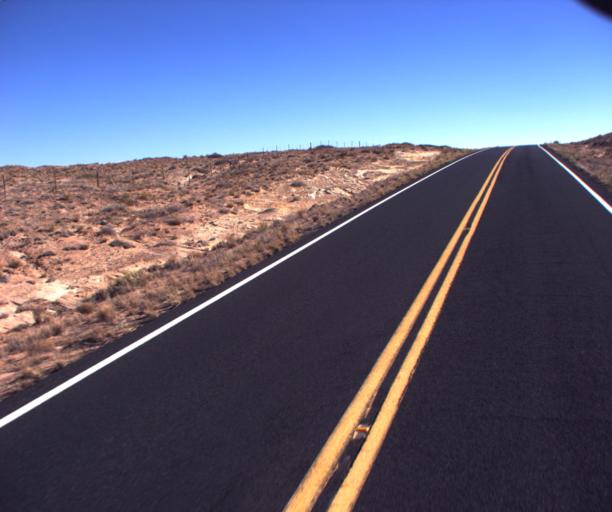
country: US
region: Arizona
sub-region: Coconino County
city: Tuba City
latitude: 36.0198
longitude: -111.1182
